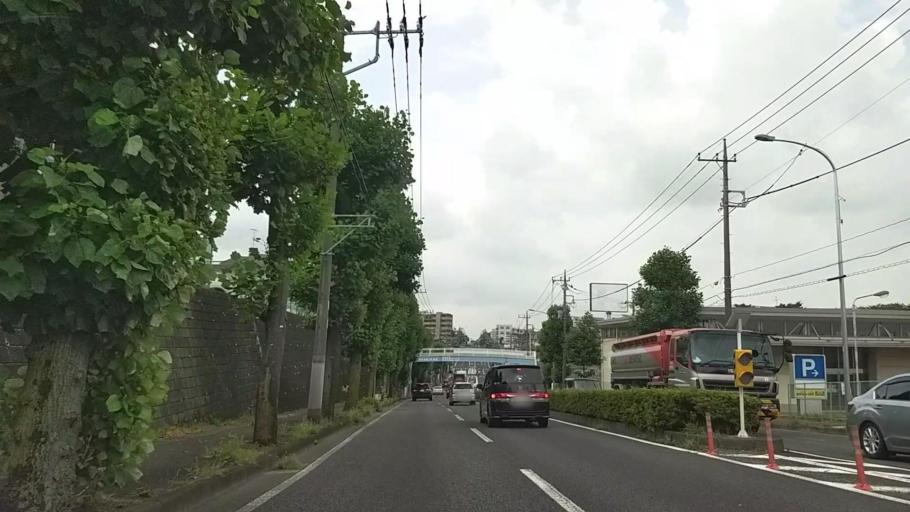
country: JP
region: Kanagawa
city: Minami-rinkan
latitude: 35.4635
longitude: 139.4874
